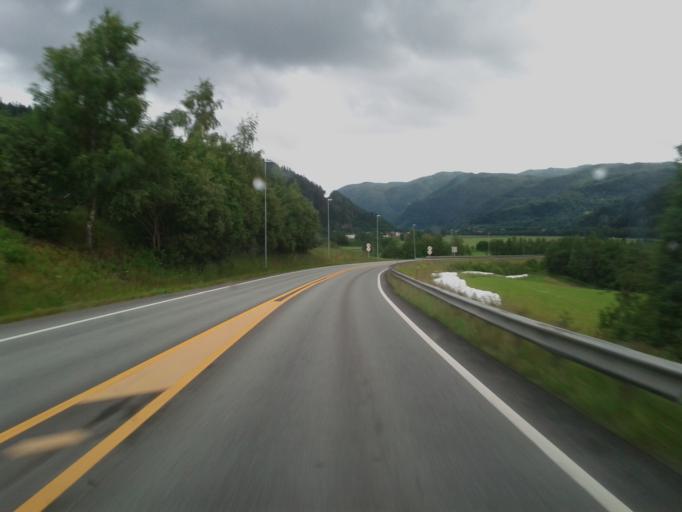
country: NO
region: Sor-Trondelag
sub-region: Melhus
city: Lundamo
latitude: 63.1077
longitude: 10.2353
